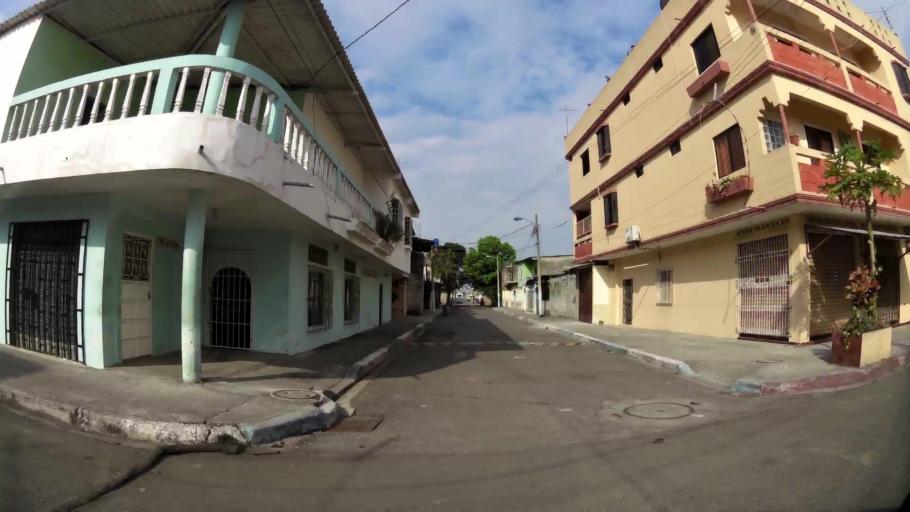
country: EC
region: Guayas
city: Guayaquil
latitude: -2.2541
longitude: -79.9051
